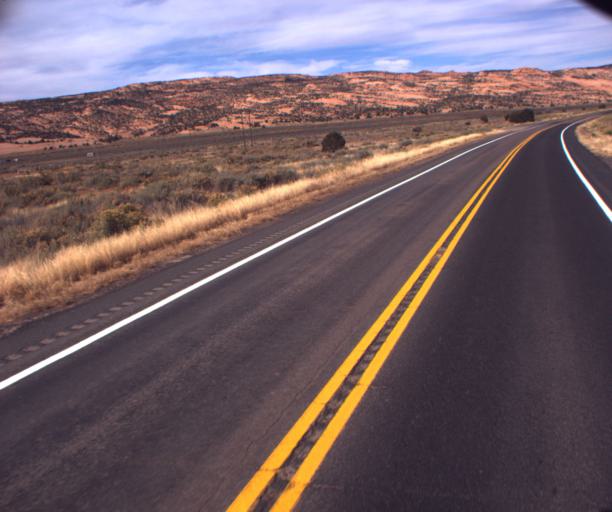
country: US
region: Arizona
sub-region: Navajo County
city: Kayenta
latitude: 36.6111
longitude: -110.4723
